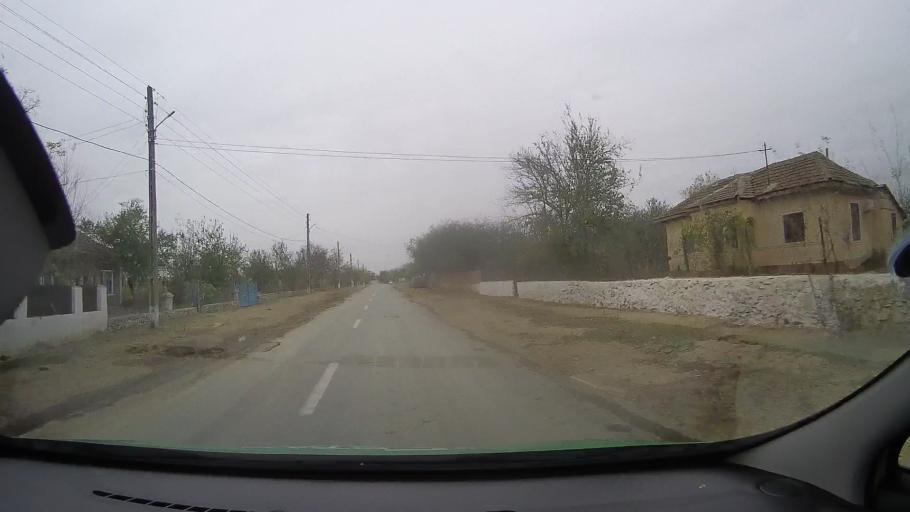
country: RO
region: Constanta
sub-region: Comuna Vulturu
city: Vulturu
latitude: 44.6433
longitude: 28.2725
